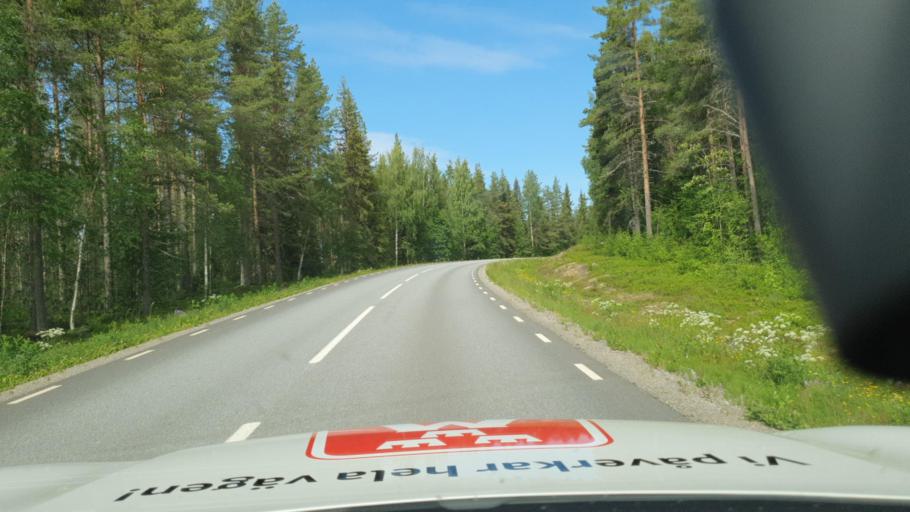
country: SE
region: Vaesterbotten
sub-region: Skelleftea Kommun
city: Forsbacka
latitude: 64.7133
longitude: 20.4226
